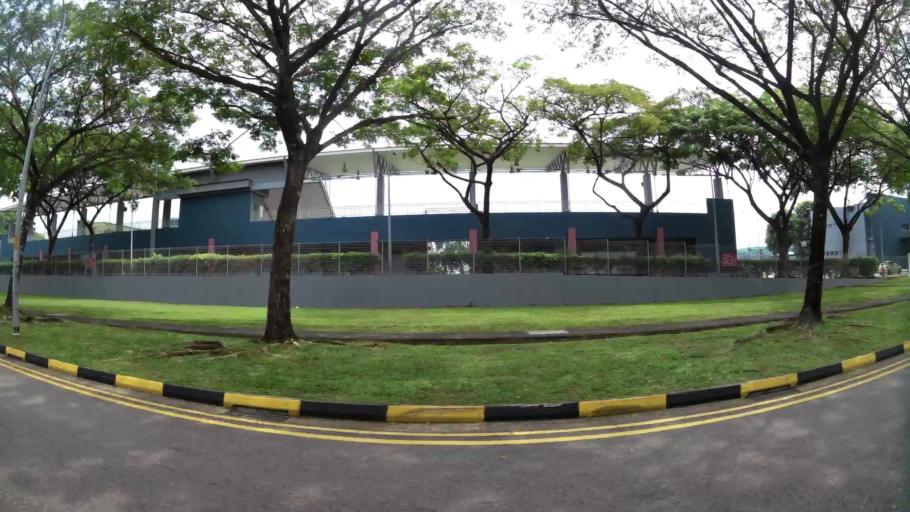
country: SG
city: Singapore
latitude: 1.3516
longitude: 103.8995
